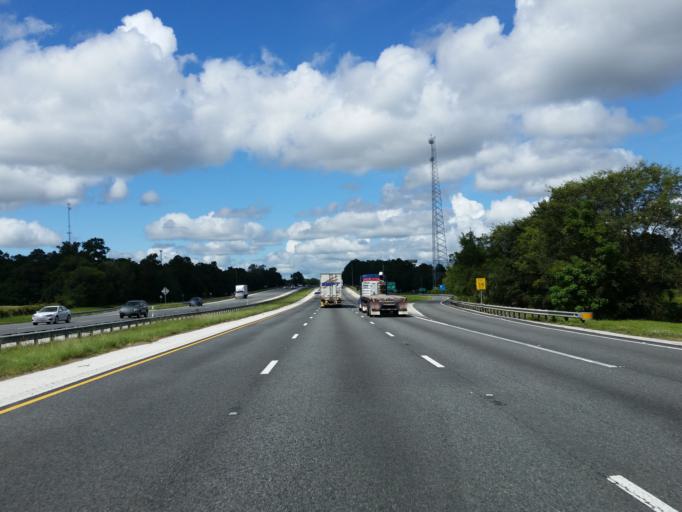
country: US
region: Florida
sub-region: Marion County
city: Citra
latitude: 29.4034
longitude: -82.2449
